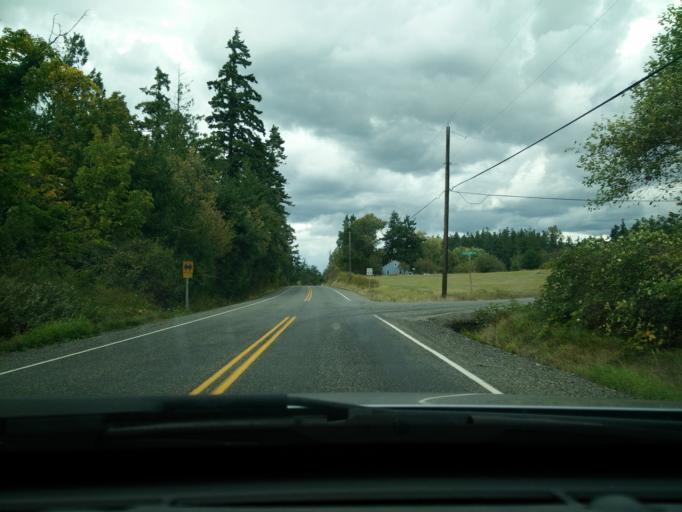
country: US
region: Washington
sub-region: Skagit County
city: Anacortes
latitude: 48.5009
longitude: -122.4818
